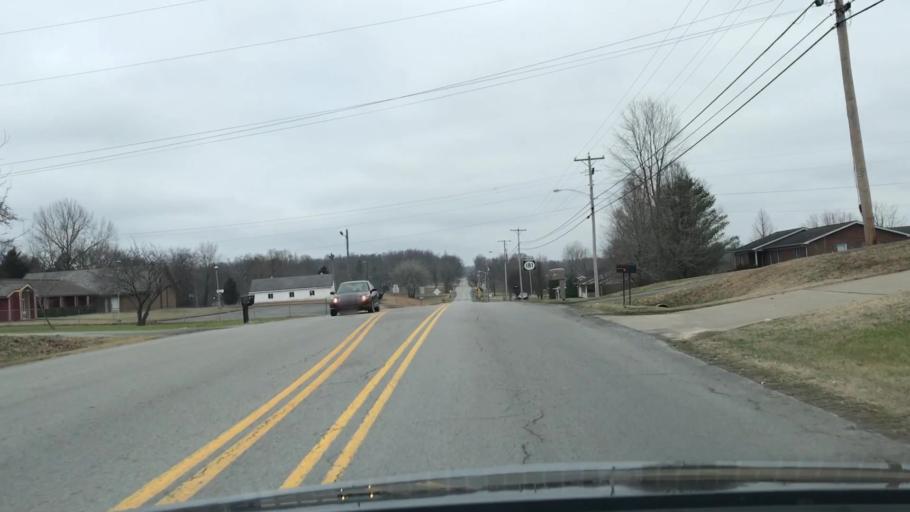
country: US
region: Kentucky
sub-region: Muhlenberg County
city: Greenville
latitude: 37.2190
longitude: -87.1939
